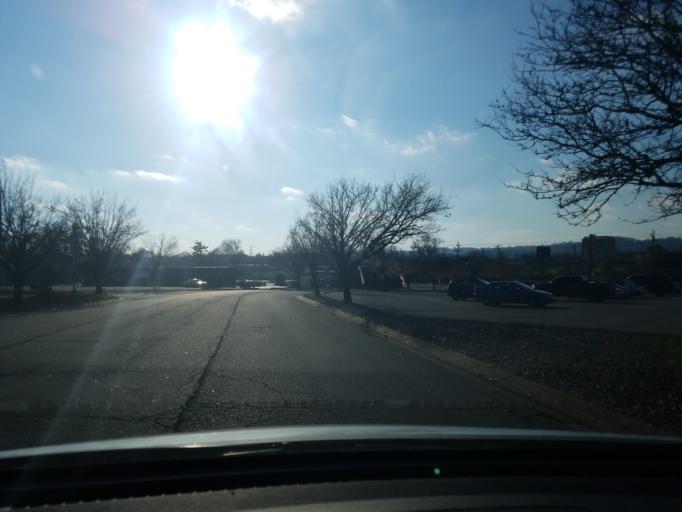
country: US
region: Indiana
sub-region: Floyd County
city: New Albany
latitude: 38.3284
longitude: -85.8174
